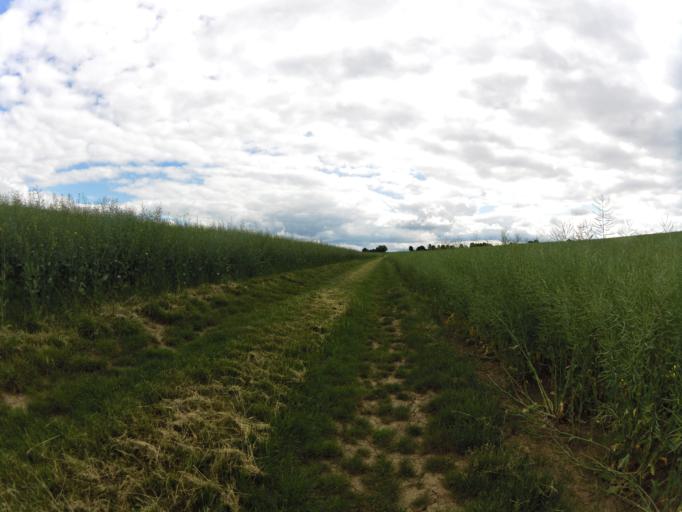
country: DE
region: Bavaria
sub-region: Regierungsbezirk Unterfranken
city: Gaukonigshofen
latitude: 49.6642
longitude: 10.0190
